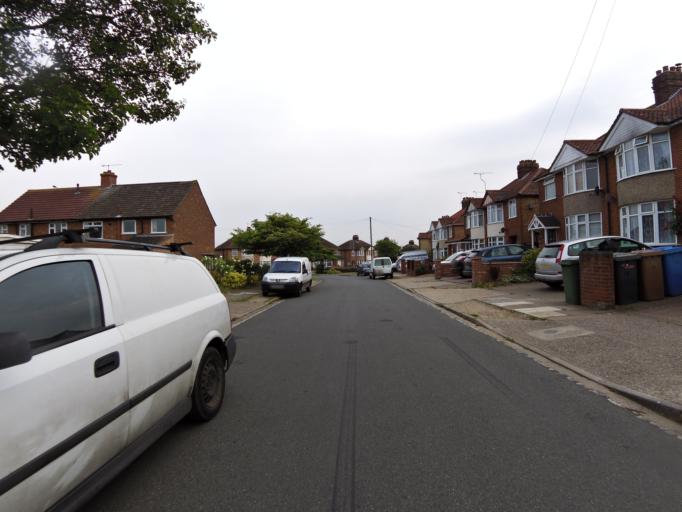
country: GB
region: England
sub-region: Suffolk
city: Ipswich
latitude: 52.0762
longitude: 1.1365
